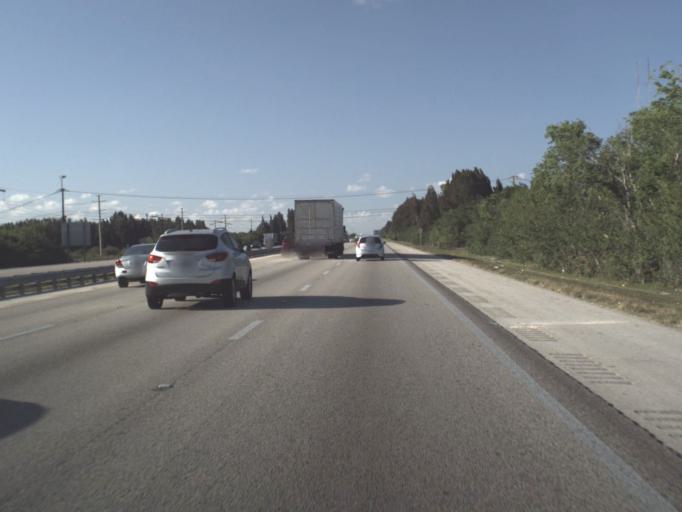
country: US
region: Florida
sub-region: Brevard County
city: June Park
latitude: 28.1289
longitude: -80.7058
